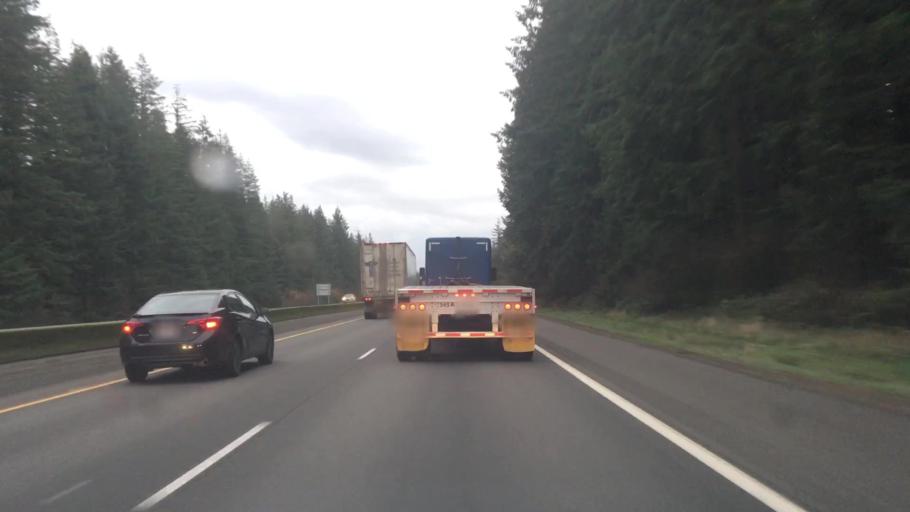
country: US
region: Washington
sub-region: Lewis County
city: Napavine
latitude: 46.5373
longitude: -122.8768
